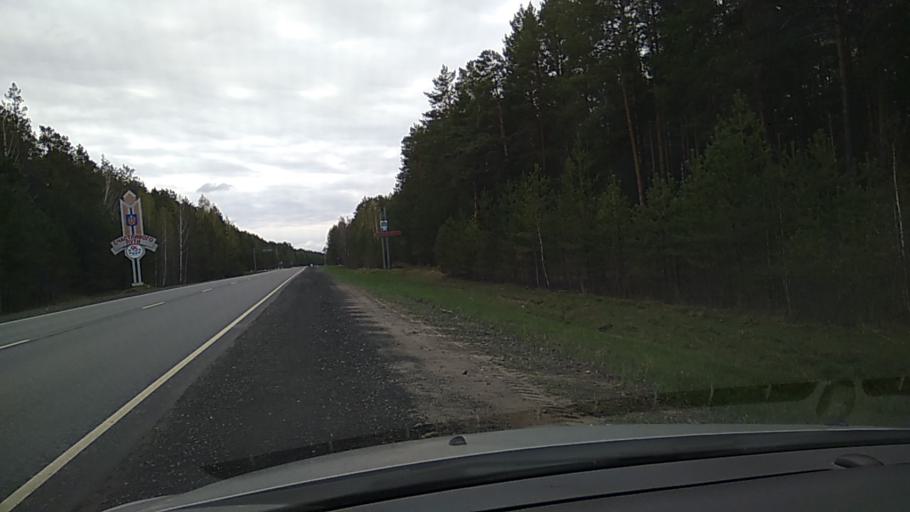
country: RU
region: Tjumen
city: Chervishevo
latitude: 56.8187
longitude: 65.3801
